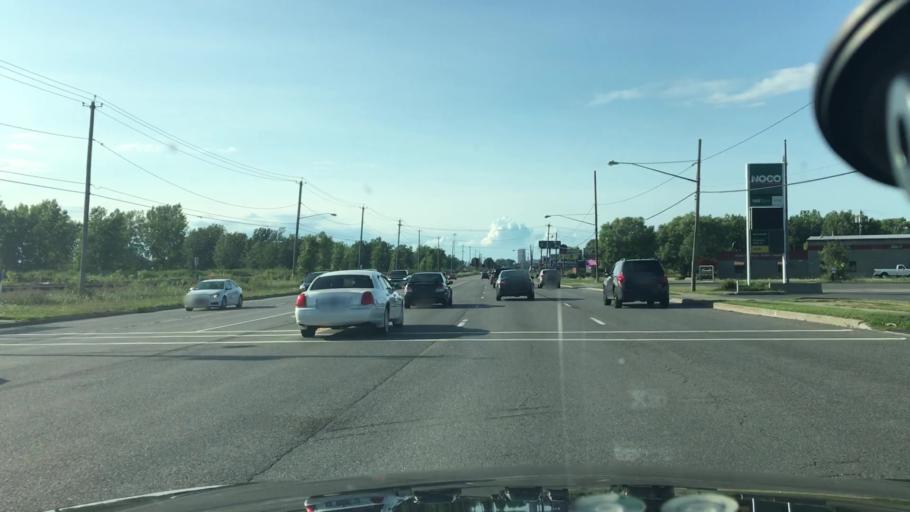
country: US
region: New York
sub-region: Erie County
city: Lackawanna
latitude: 42.8159
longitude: -78.8460
